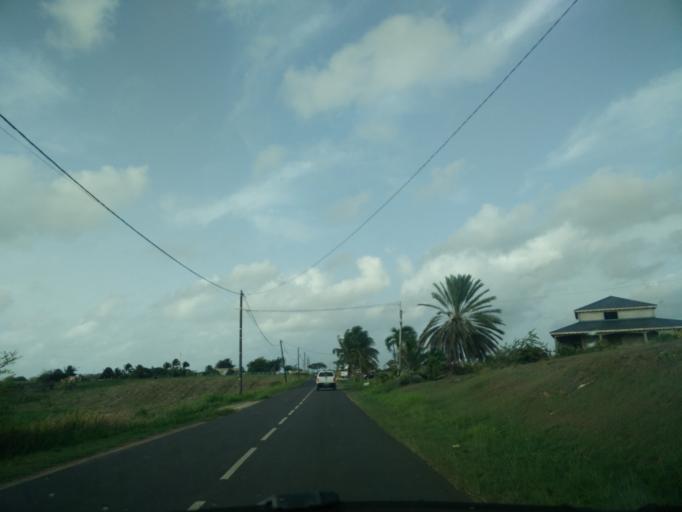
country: GP
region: Guadeloupe
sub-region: Guadeloupe
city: Le Moule
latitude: 16.3099
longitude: -61.3667
